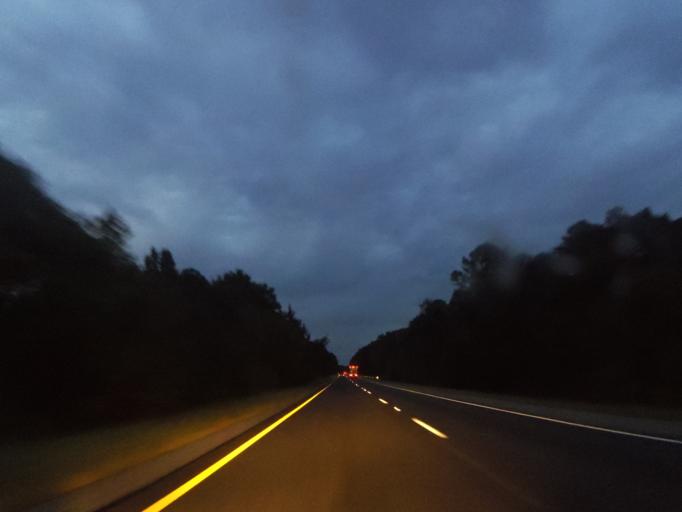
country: US
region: Alabama
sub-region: DeKalb County
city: Collinsville
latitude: 34.3055
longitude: -85.8565
